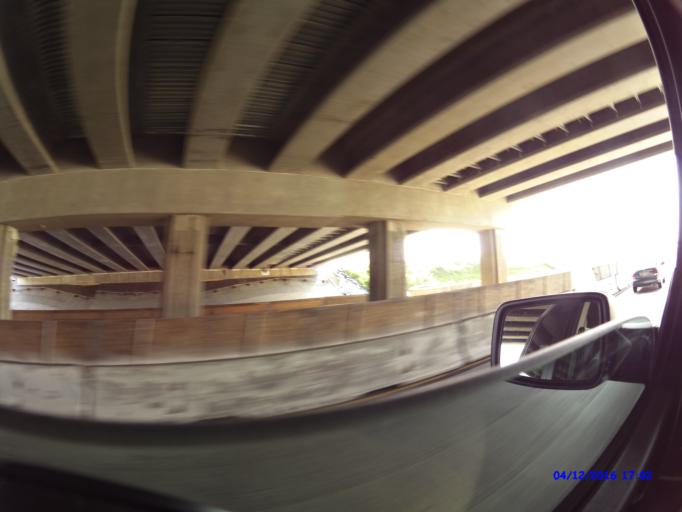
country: US
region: California
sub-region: Stanislaus County
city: Salida
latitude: 37.7090
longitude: -121.0809
